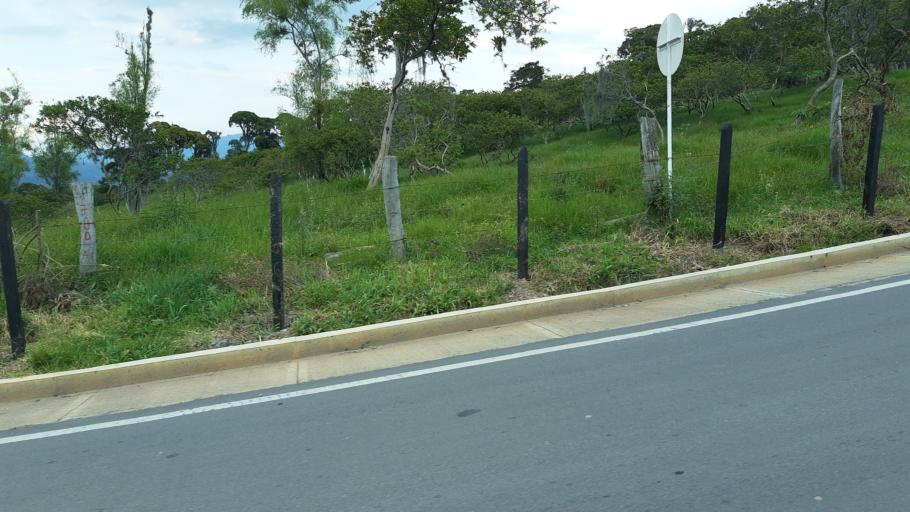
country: CO
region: Boyaca
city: Moniquira
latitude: 5.8075
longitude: -73.5990
